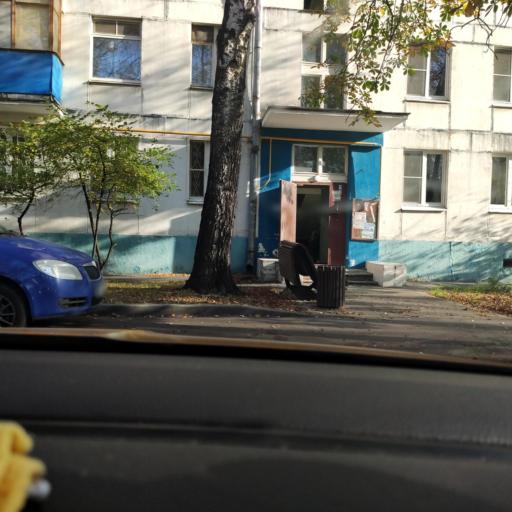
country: RU
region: Moskovskaya
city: Alekseyevka
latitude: 55.6365
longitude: 37.7996
